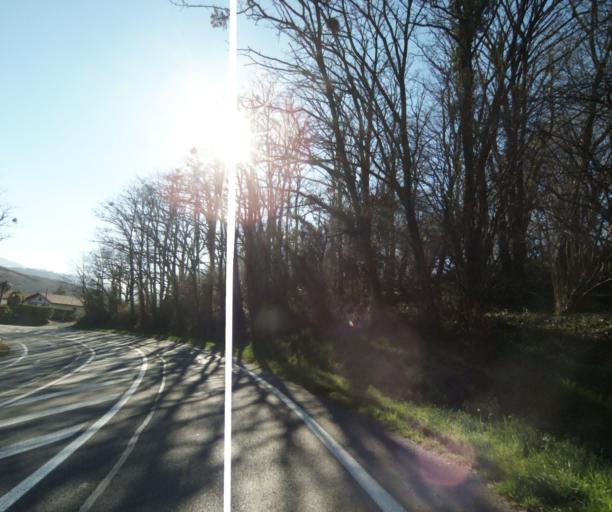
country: FR
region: Aquitaine
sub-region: Departement des Pyrenees-Atlantiques
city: Hendaye
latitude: 43.3501
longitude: -1.7483
